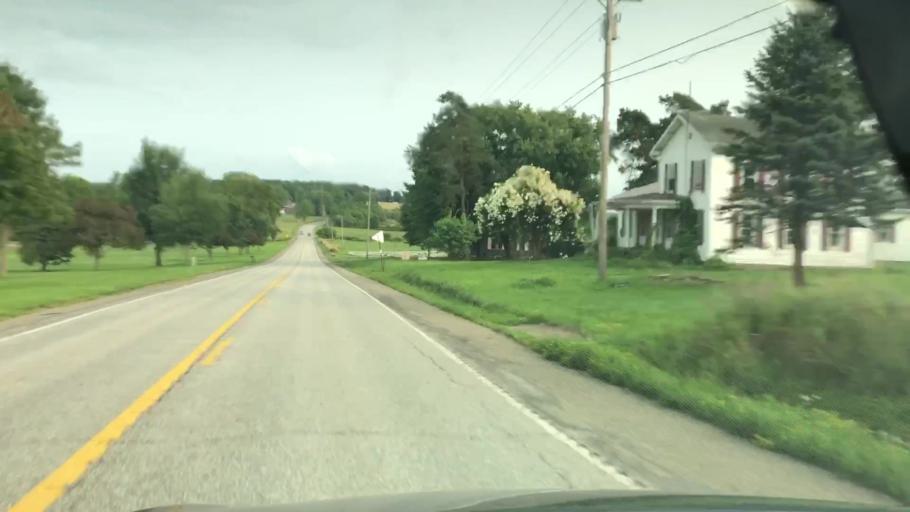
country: US
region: Pennsylvania
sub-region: Erie County
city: Union City
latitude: 41.8556
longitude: -79.8277
